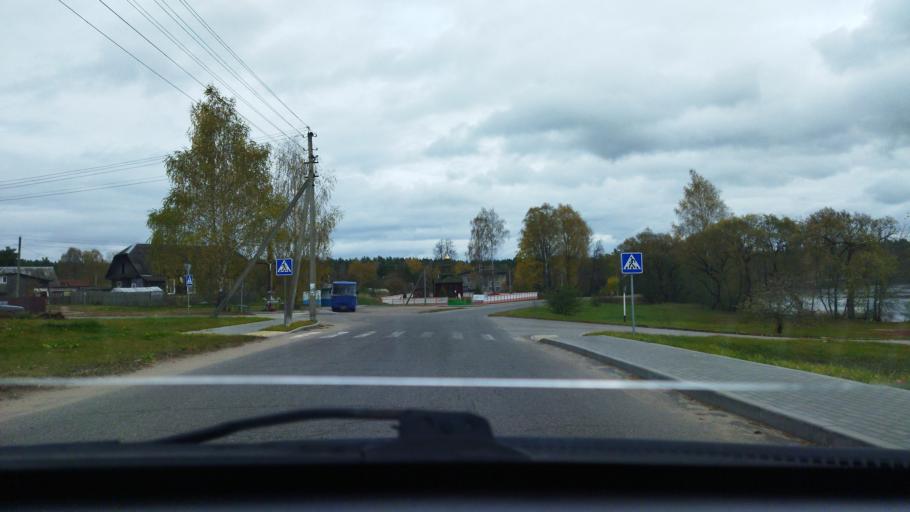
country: BY
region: Minsk
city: Svir
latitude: 54.8079
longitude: 26.2320
